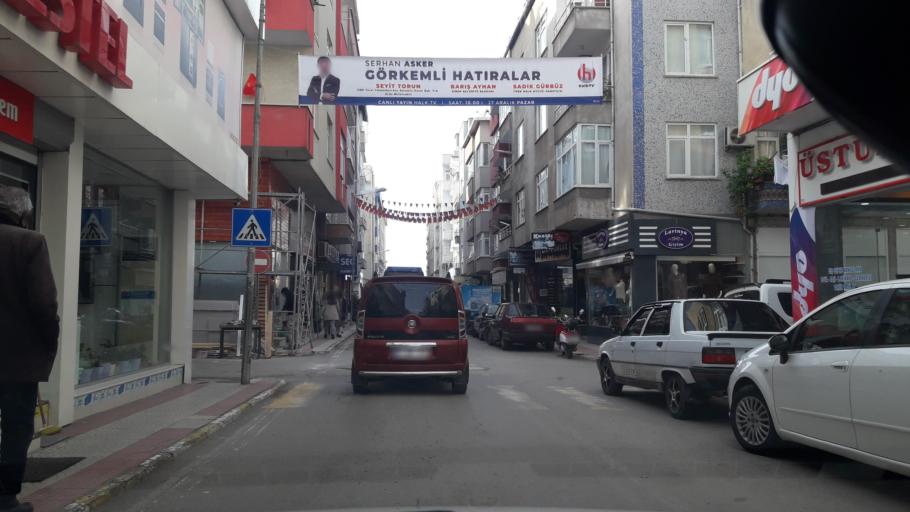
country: TR
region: Sinop
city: Sinop
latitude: 42.0267
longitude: 35.1467
